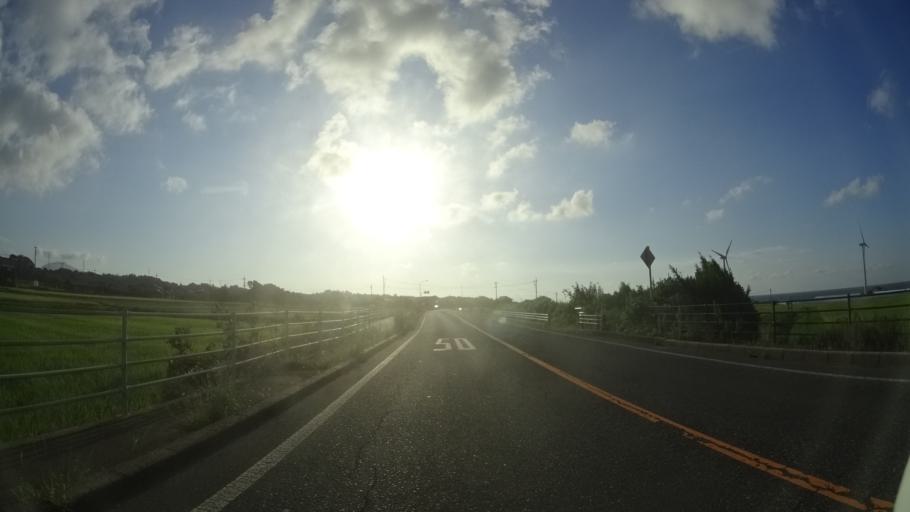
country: JP
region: Tottori
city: Yonago
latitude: 35.5205
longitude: 133.5629
